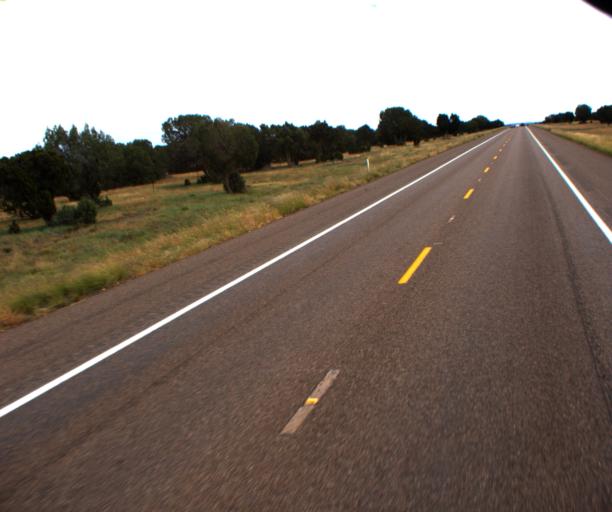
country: US
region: Arizona
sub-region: Navajo County
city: Show Low
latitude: 34.2991
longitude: -110.0345
